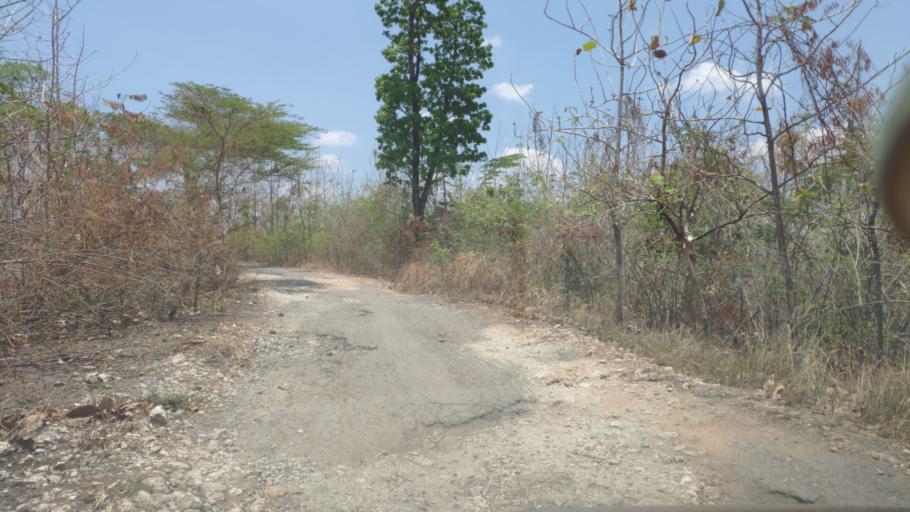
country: ID
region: Central Java
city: Randublatung
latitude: -7.2714
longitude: 111.3781
